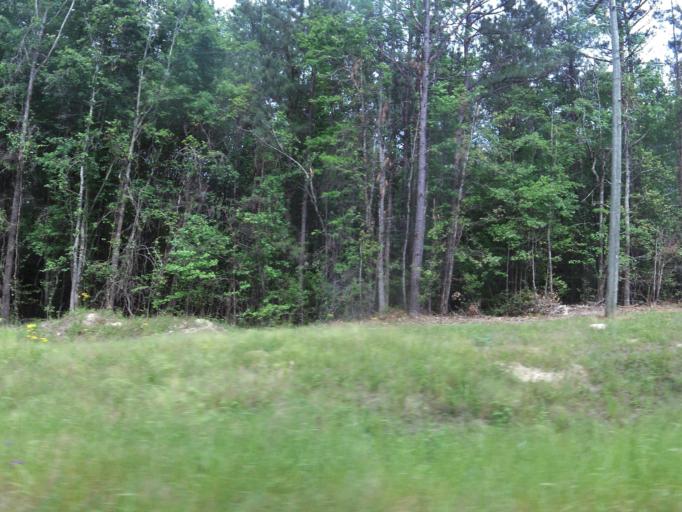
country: US
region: Georgia
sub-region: McDuffie County
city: Thomson
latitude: 33.3361
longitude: -82.4564
